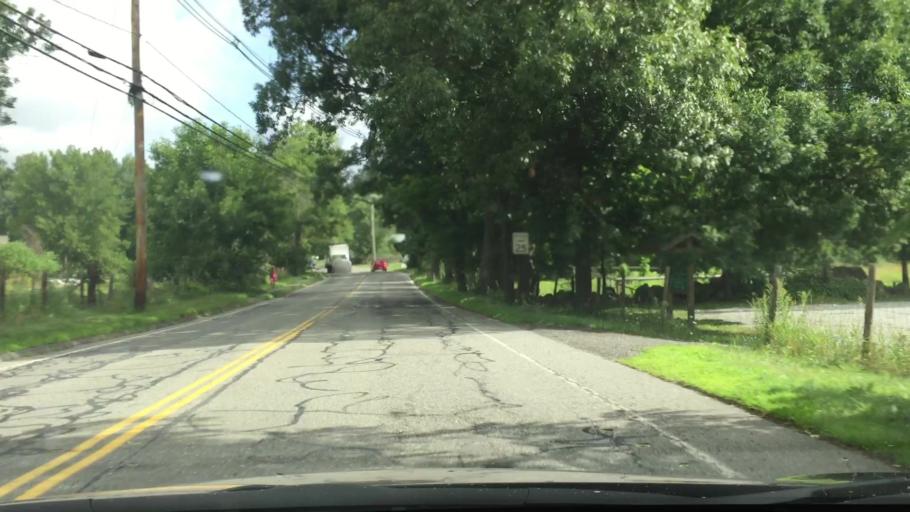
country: US
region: Massachusetts
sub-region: Middlesex County
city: Littleton Common
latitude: 42.5256
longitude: -71.4591
